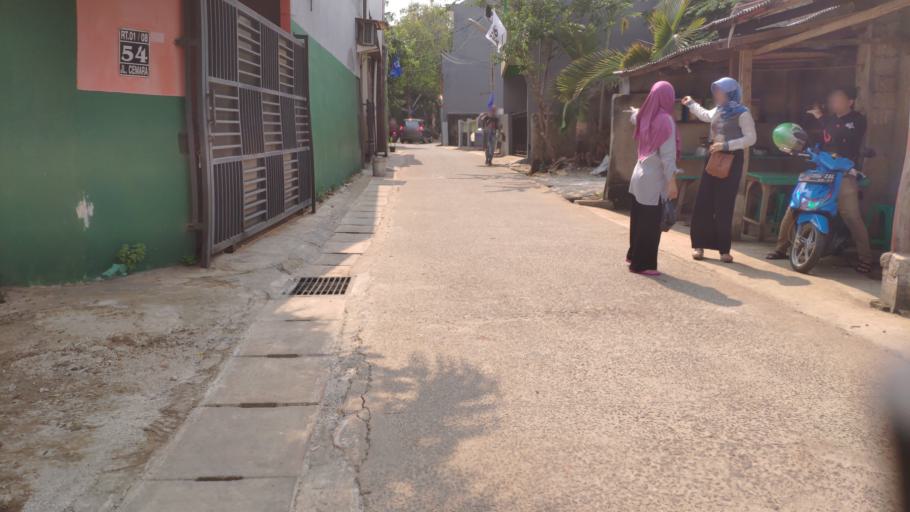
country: ID
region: West Java
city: Sawangan
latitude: -6.3822
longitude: 106.7949
